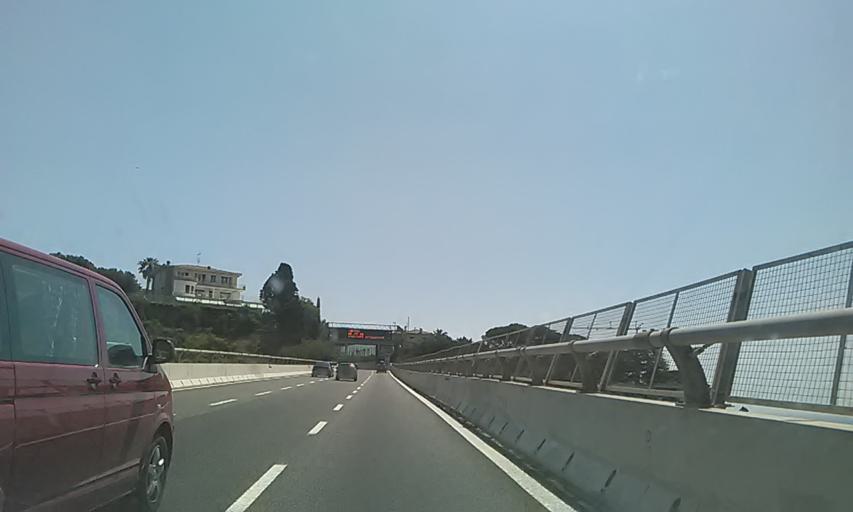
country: IT
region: Liguria
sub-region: Provincia di Savona
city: Varazze
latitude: 44.3626
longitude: 8.5889
